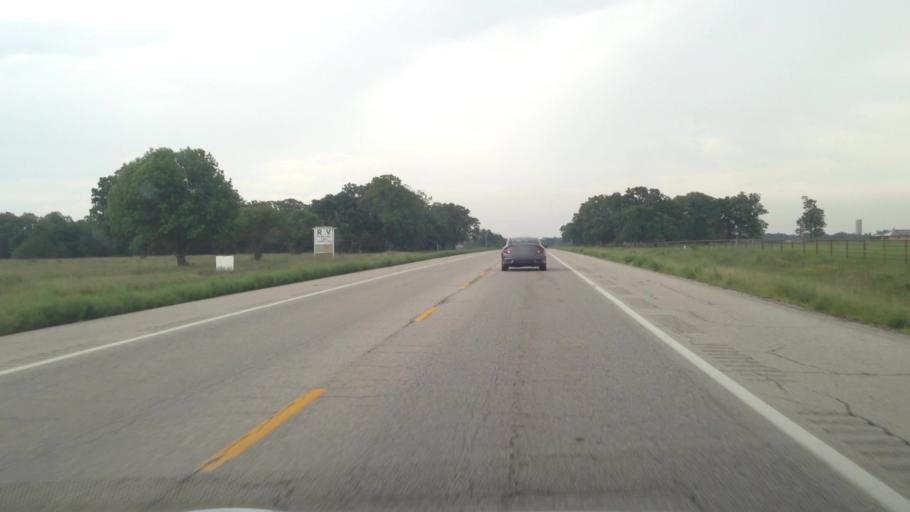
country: US
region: Kansas
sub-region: Cherokee County
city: Galena
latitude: 37.0157
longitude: -94.6336
